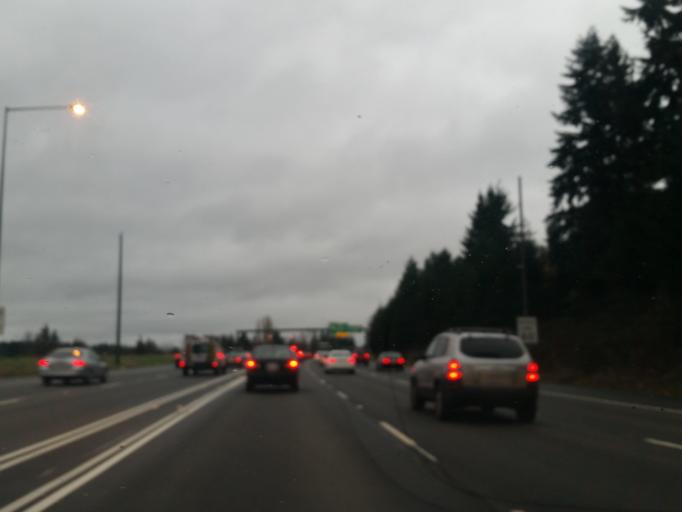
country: US
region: Washington
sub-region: King County
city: Kingsgate
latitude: 47.7235
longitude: -122.1891
